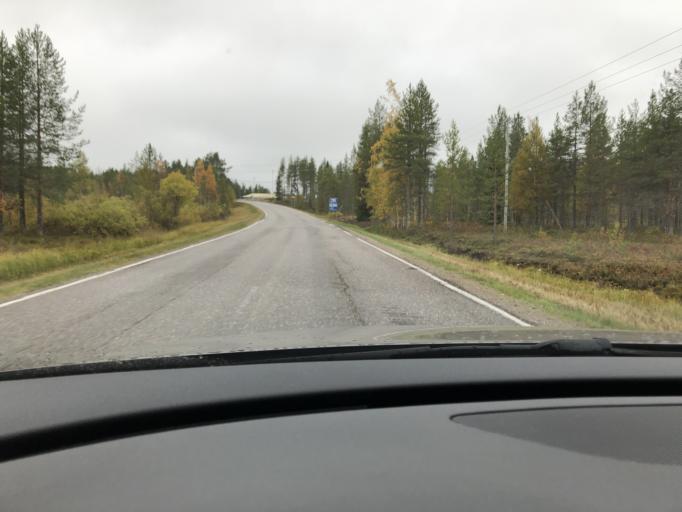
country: FI
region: Lapland
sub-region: Itae-Lappi
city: Posio
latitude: 66.1207
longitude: 28.1832
